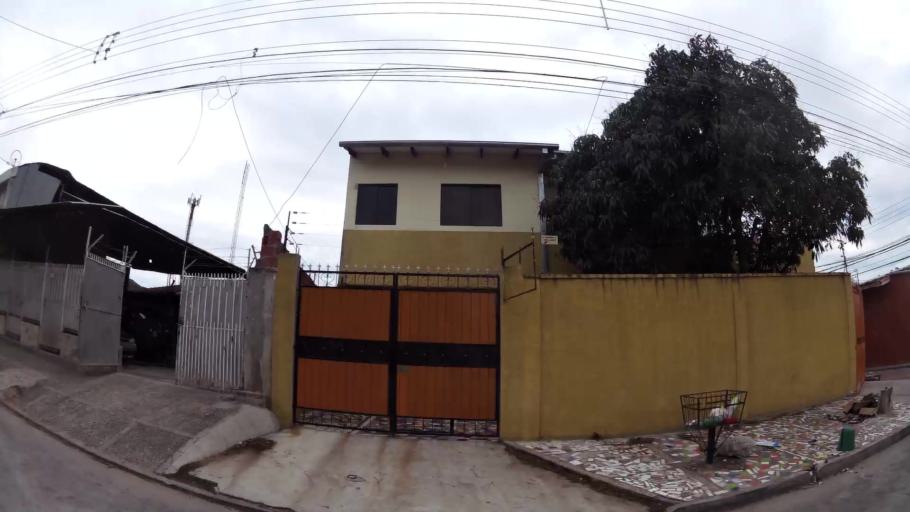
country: BO
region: Santa Cruz
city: Santa Cruz de la Sierra
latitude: -17.7726
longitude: -63.1569
